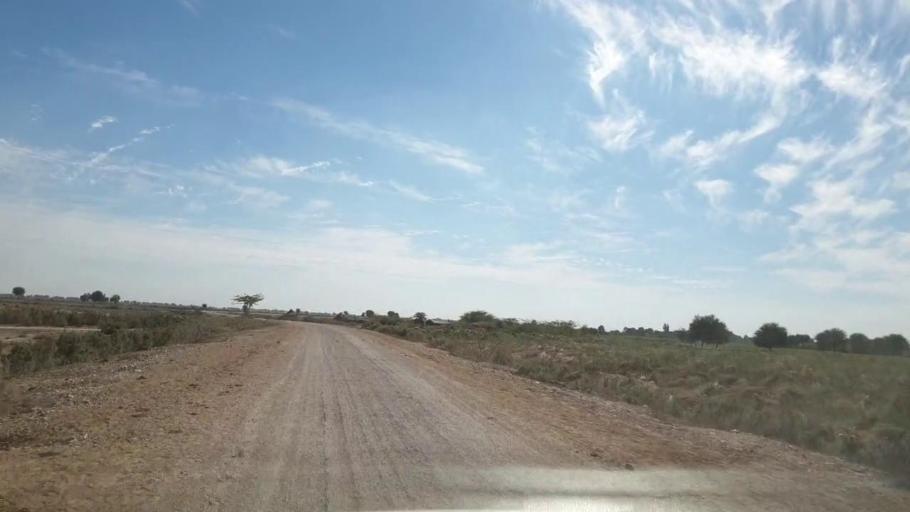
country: PK
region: Sindh
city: Pithoro
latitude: 25.5740
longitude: 69.3049
